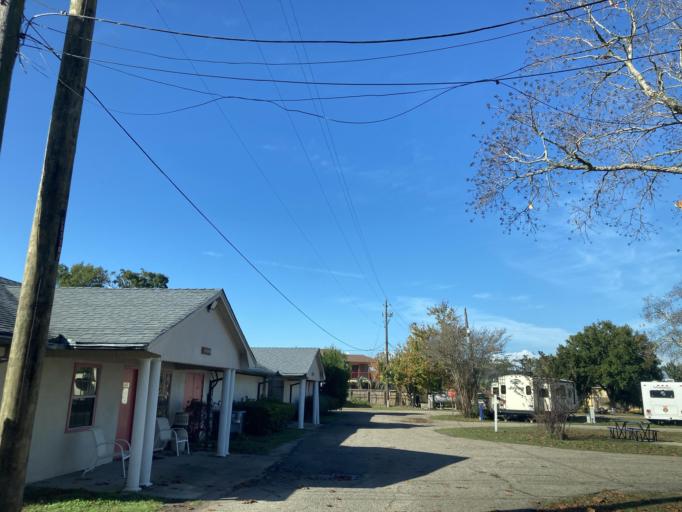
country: US
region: Mississippi
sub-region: Harrison County
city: Biloxi
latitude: 30.3957
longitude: -88.9429
